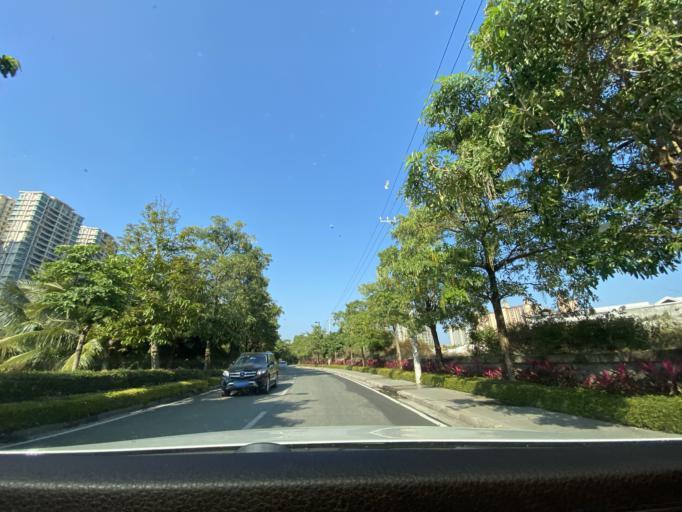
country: CN
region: Hainan
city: Yingzhou
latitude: 18.4101
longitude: 109.8812
